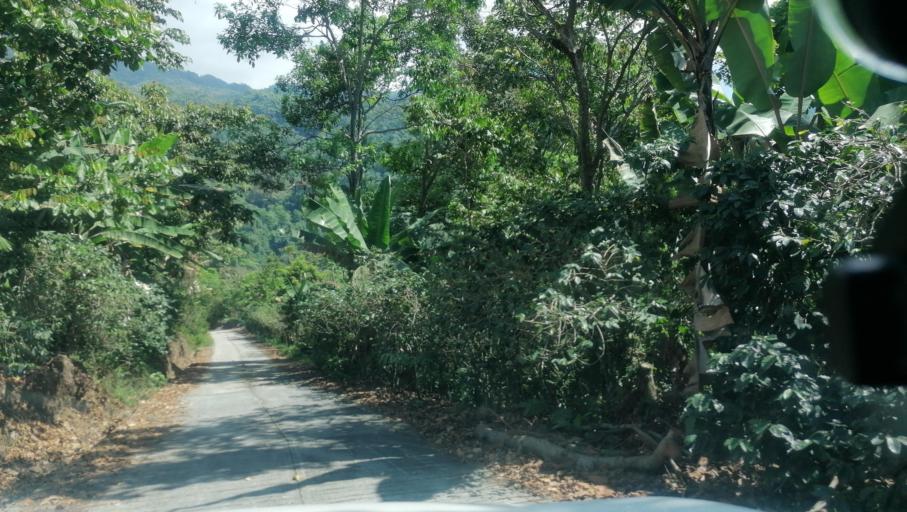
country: MX
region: Chiapas
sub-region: Union Juarez
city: Santo Domingo
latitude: 15.0773
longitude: -92.1296
